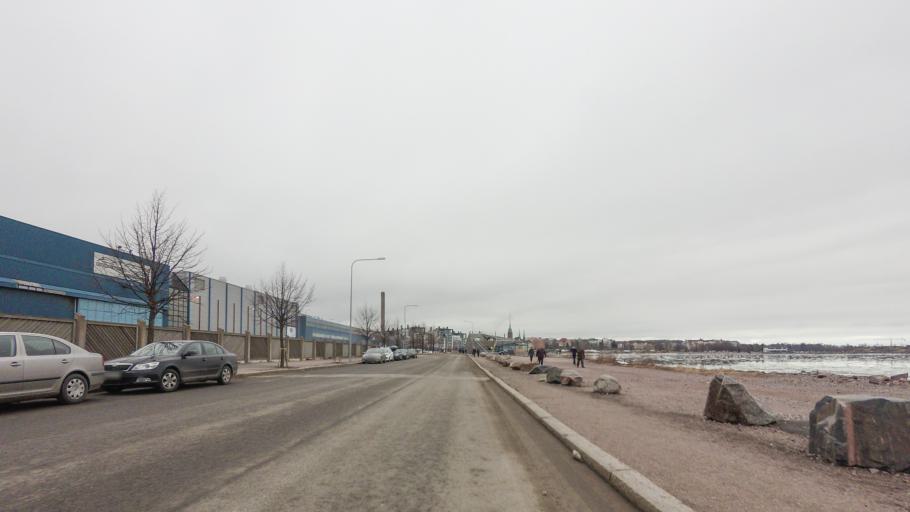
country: FI
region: Uusimaa
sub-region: Helsinki
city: Helsinki
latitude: 60.1509
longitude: 24.9289
